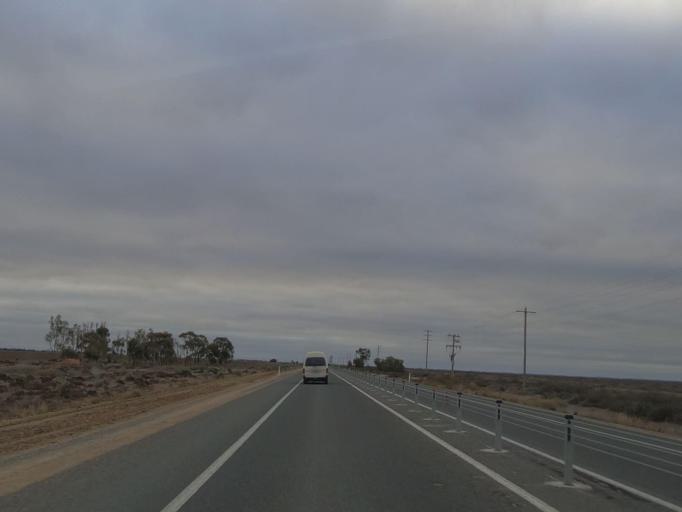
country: AU
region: Victoria
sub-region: Swan Hill
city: Swan Hill
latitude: -35.5189
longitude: 143.7301
